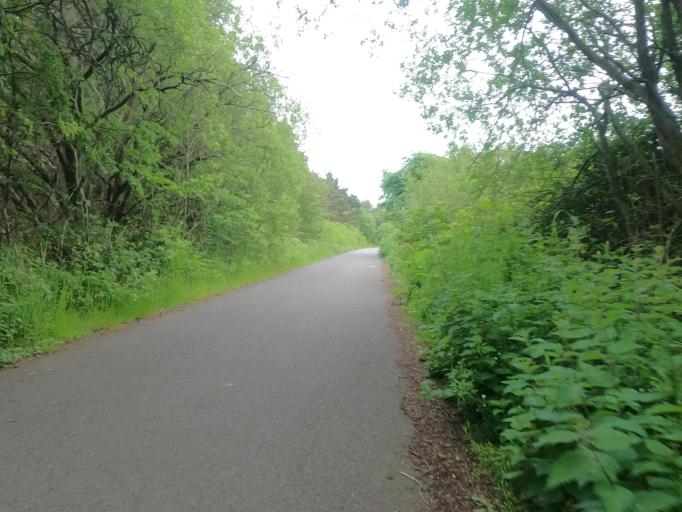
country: GB
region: England
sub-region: Northumberland
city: Bedlington
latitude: 55.1223
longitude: -1.5640
